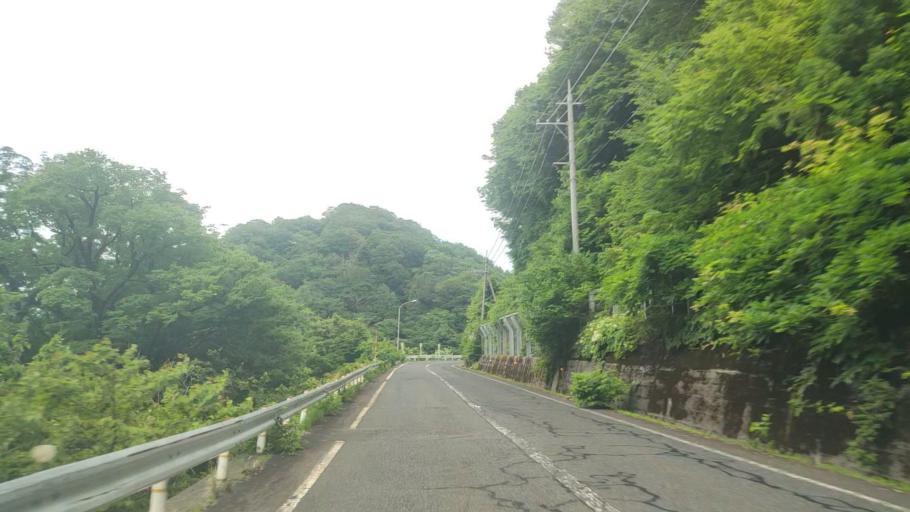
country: JP
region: Tottori
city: Kurayoshi
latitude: 35.3198
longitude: 134.0086
